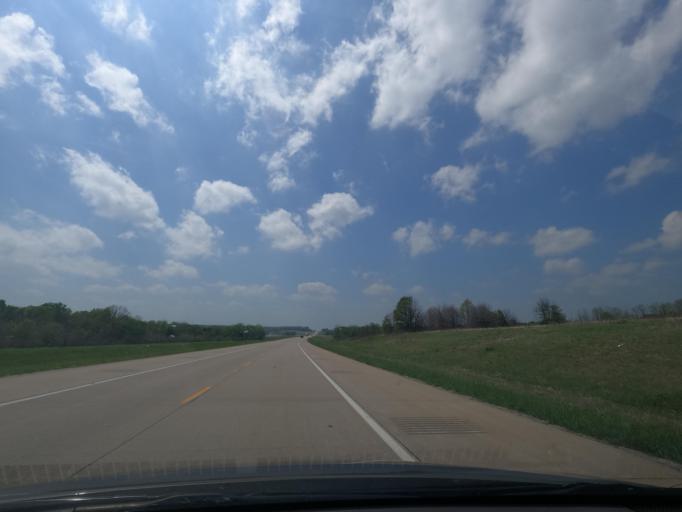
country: US
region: Kansas
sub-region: Wilson County
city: Fredonia
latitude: 37.6141
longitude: -95.9364
